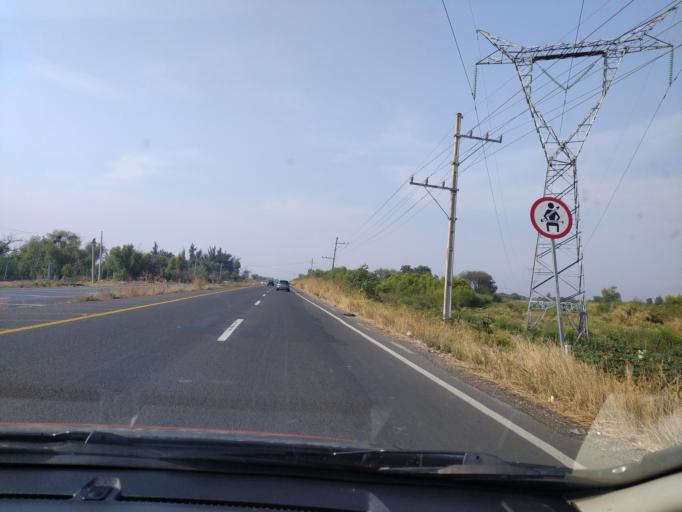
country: MX
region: Jalisco
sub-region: Acatlan de Juarez
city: Villa de los Ninos
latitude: 20.3927
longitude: -103.5934
